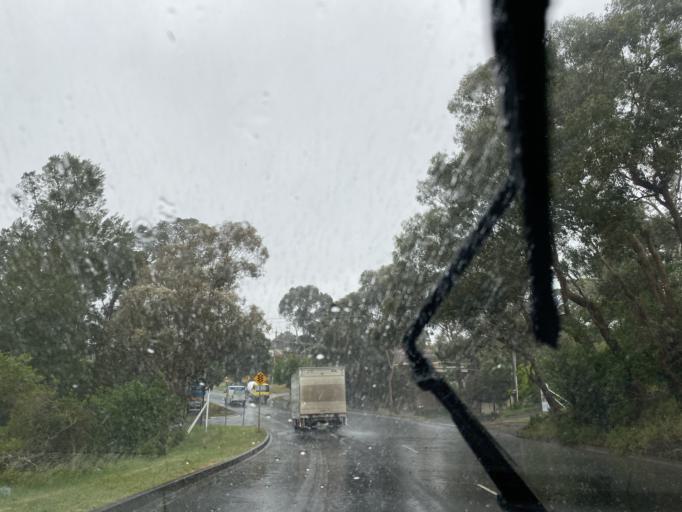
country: AU
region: Victoria
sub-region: Banyule
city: Montmorency
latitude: -37.7157
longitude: 145.1152
